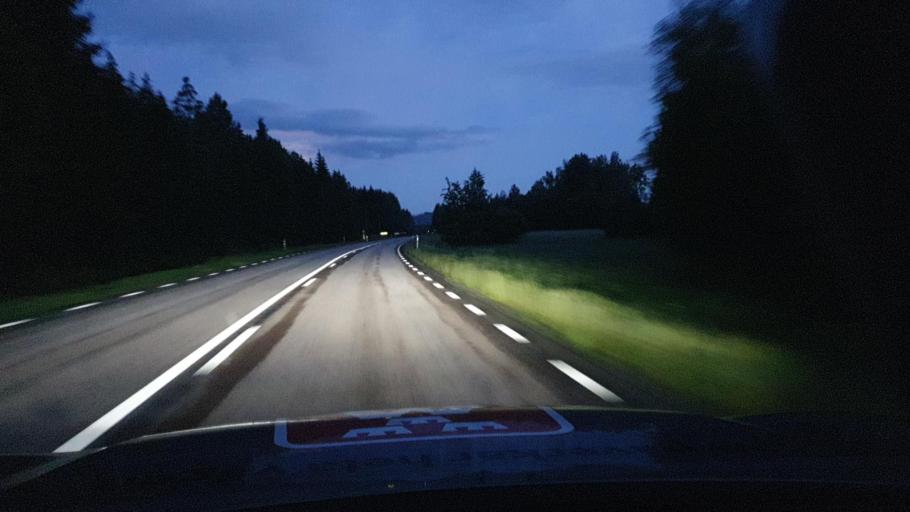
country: SE
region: OErebro
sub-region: Karlskoga Kommun
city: Karlskoga
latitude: 59.4234
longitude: 14.4280
